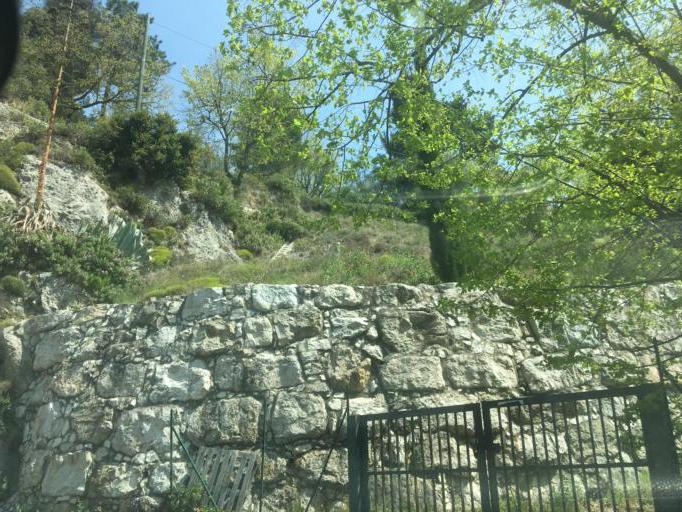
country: FR
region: Provence-Alpes-Cote d'Azur
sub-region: Departement des Alpes-Maritimes
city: Saint-Martin-du-Var
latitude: 43.8296
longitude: 7.2055
